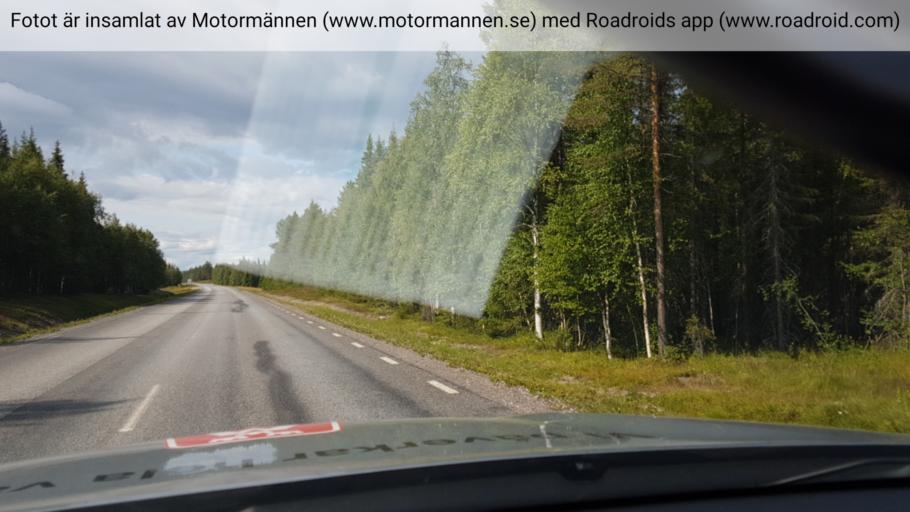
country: SE
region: Norrbotten
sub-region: Arvidsjaurs Kommun
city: Arvidsjaur
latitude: 65.5888
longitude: 19.4552
